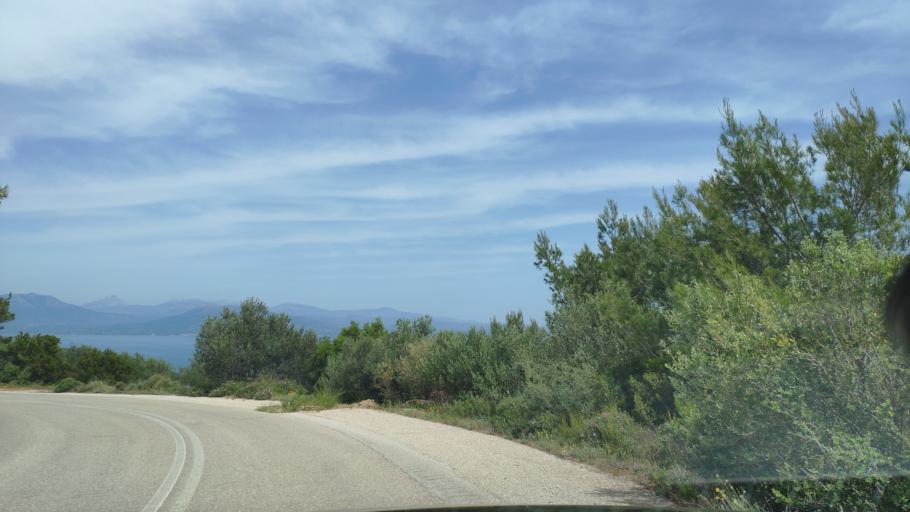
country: GR
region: Attica
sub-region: Nomarchia Anatolikis Attikis
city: Grammatiko
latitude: 38.2532
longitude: 23.9692
